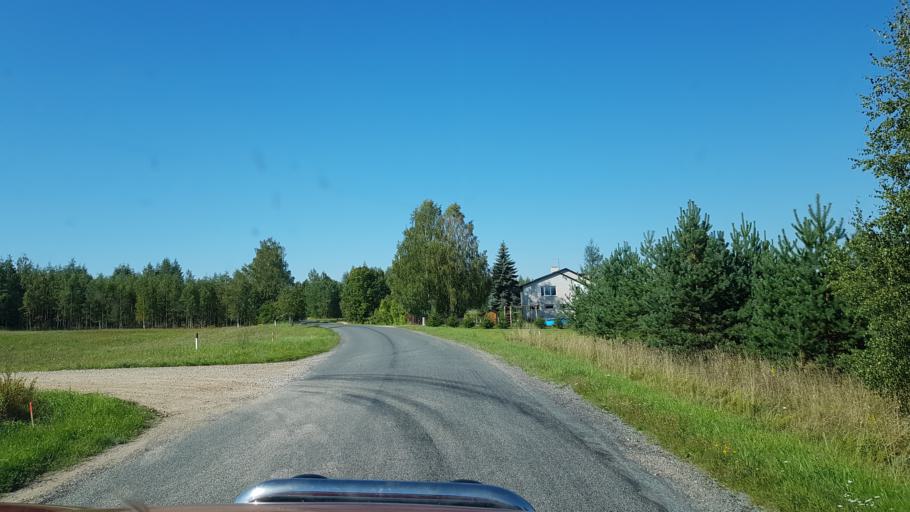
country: EE
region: Tartu
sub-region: Tartu linn
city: Tartu
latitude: 58.3500
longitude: 26.9045
